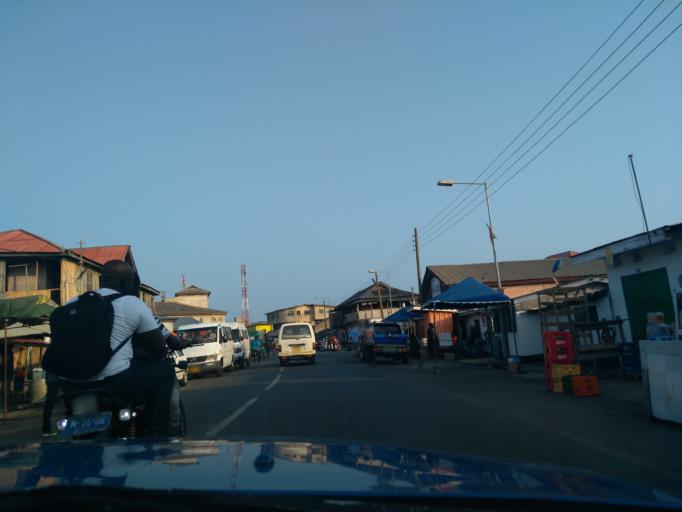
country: GH
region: Greater Accra
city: Accra
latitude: 5.5383
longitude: -0.2130
